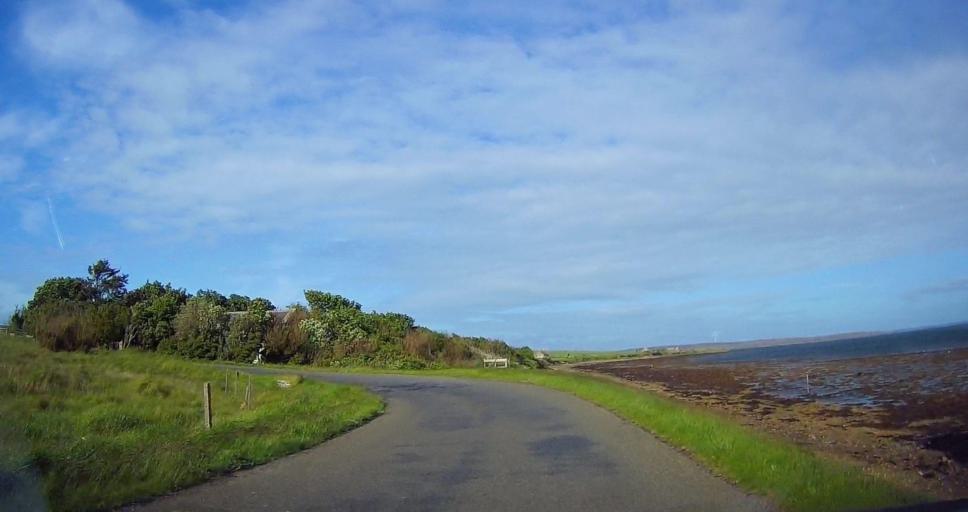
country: GB
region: Scotland
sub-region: Orkney Islands
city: Stromness
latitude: 58.8173
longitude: -3.2027
